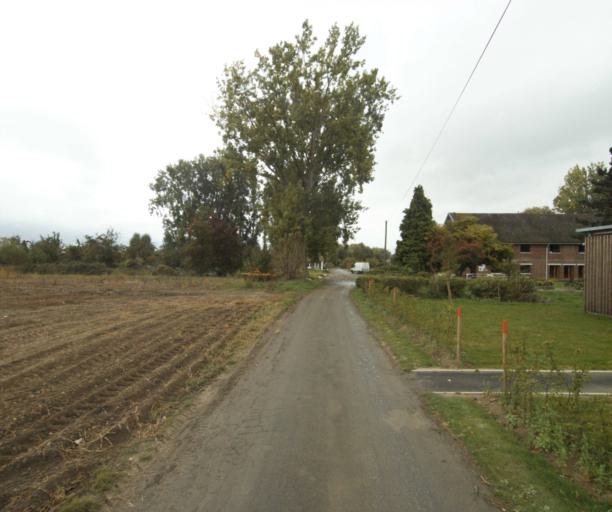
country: FR
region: Nord-Pas-de-Calais
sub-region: Departement du Nord
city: Wavrin
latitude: 50.5879
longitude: 2.9425
